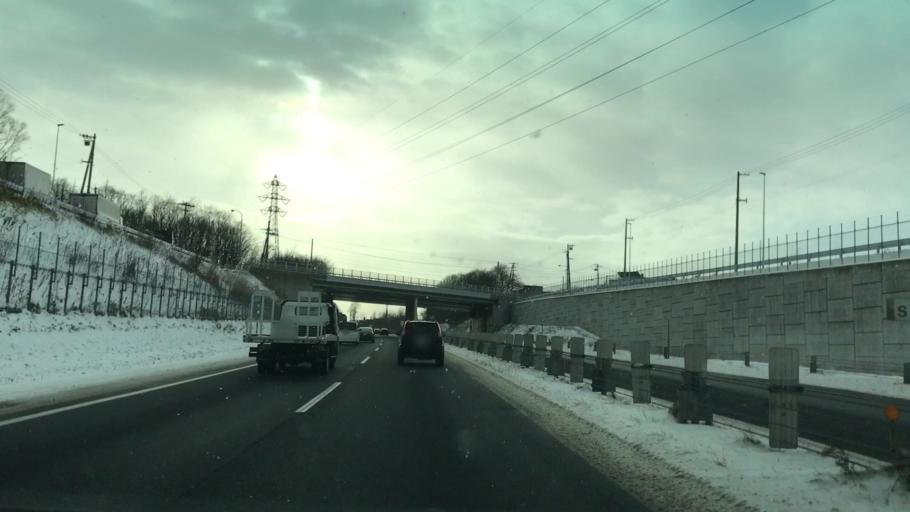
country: JP
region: Hokkaido
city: Kitahiroshima
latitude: 42.9851
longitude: 141.4717
